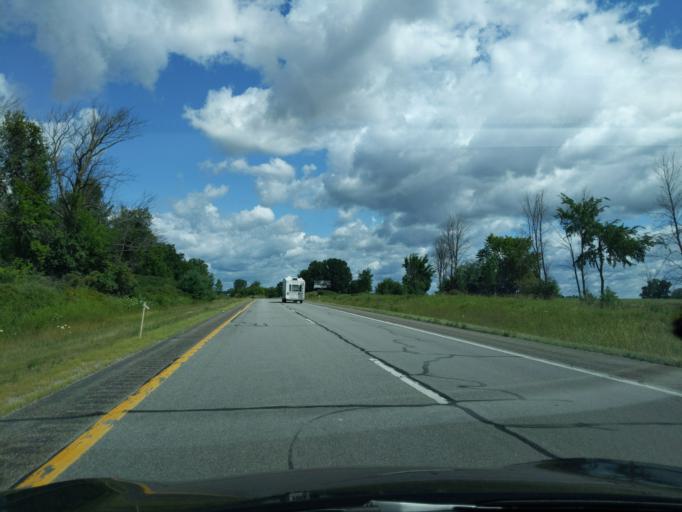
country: US
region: Michigan
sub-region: Clare County
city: Clare
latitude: 43.7506
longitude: -84.7574
